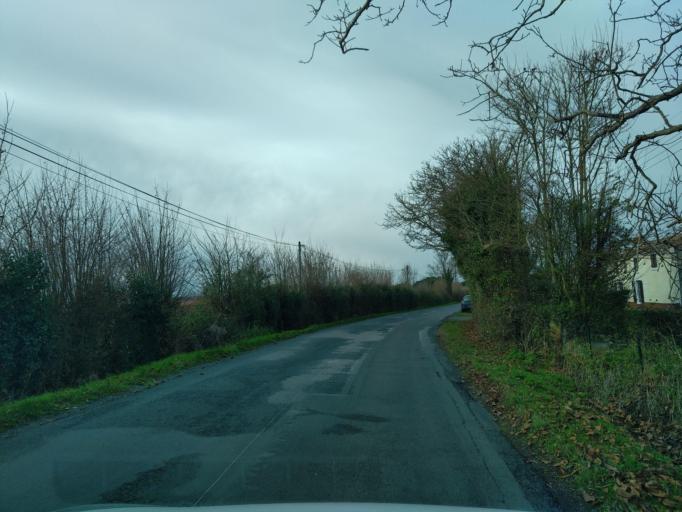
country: FR
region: Pays de la Loire
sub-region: Departement de la Vendee
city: Vix
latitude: 46.3490
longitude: -0.8334
